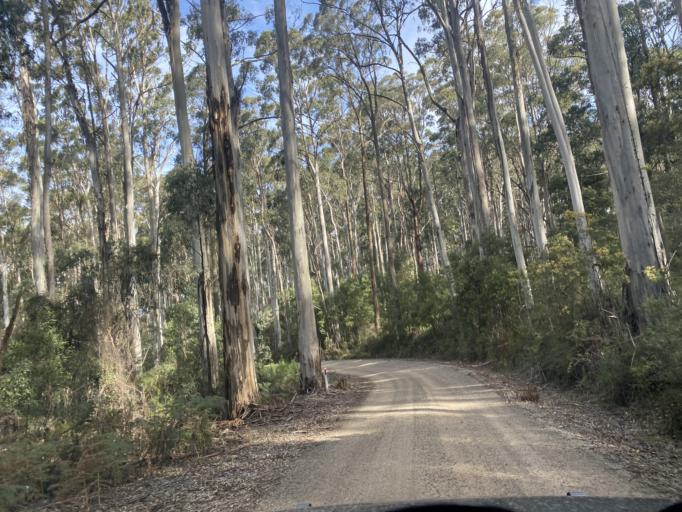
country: AU
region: Victoria
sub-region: Mansfield
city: Mansfield
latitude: -36.8527
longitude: 146.1892
